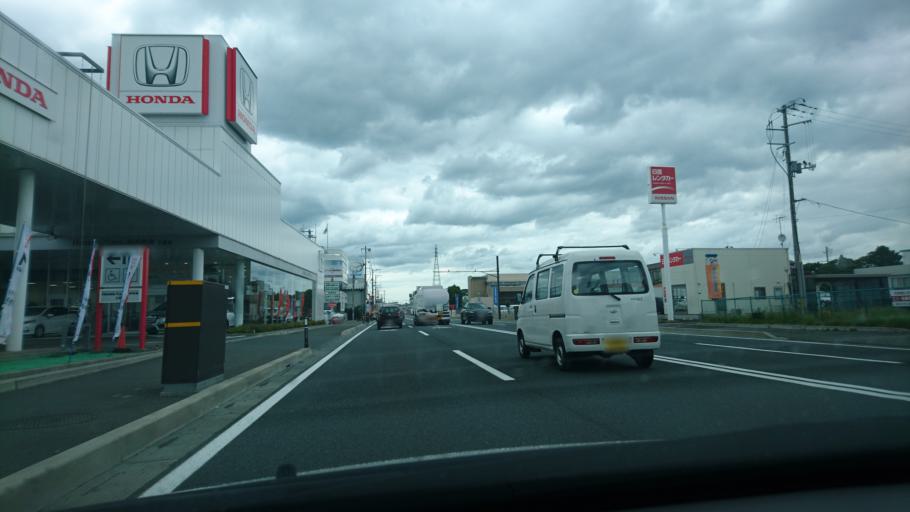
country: JP
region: Iwate
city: Morioka-shi
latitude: 39.7320
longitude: 141.1232
